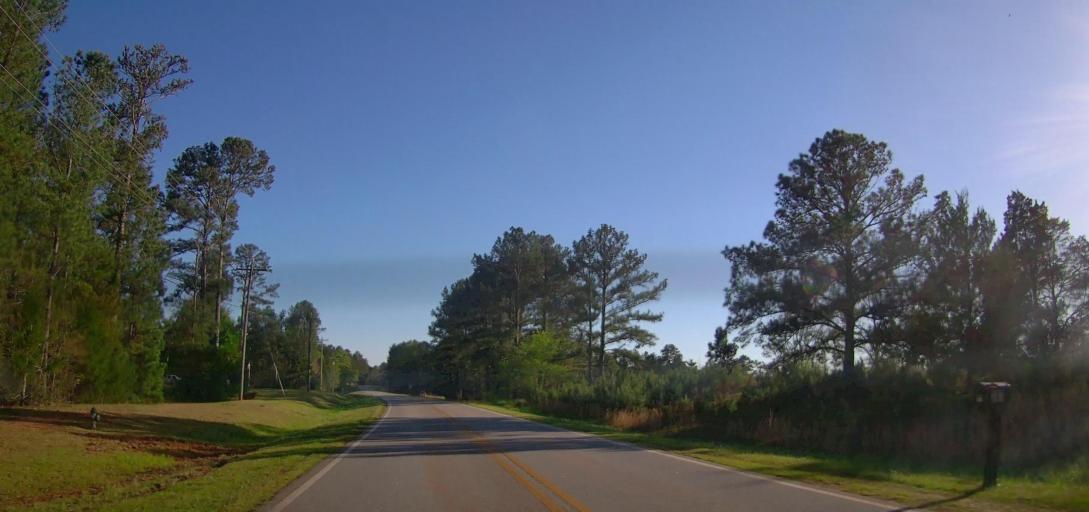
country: US
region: Georgia
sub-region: Butts County
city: Indian Springs
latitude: 33.2819
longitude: -83.8966
